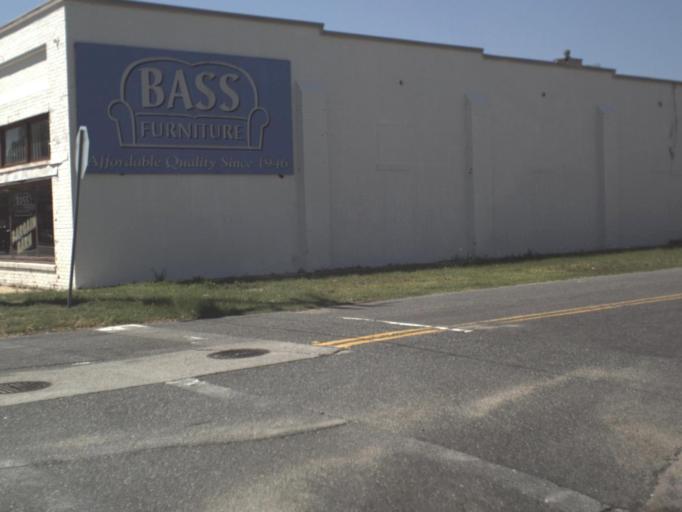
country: US
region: Florida
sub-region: Escambia County
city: Pensacola
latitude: 30.4210
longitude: -87.2478
